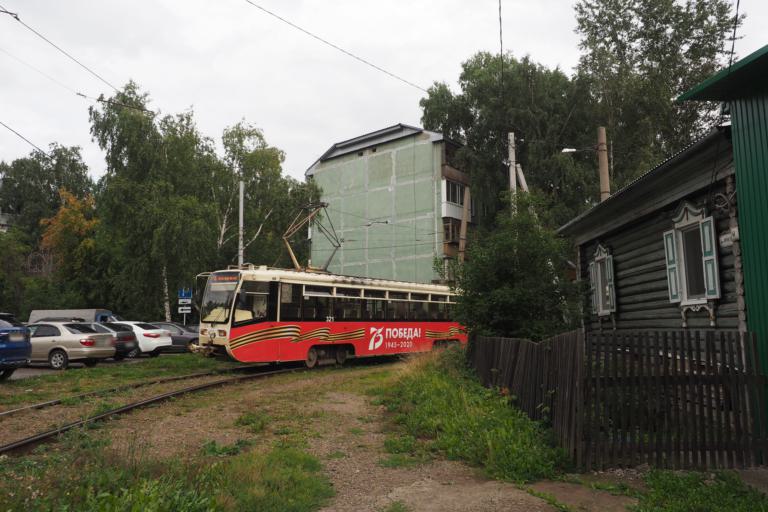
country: RU
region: Tomsk
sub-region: Tomskiy Rayon
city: Tomsk
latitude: 56.4784
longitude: 85.0101
